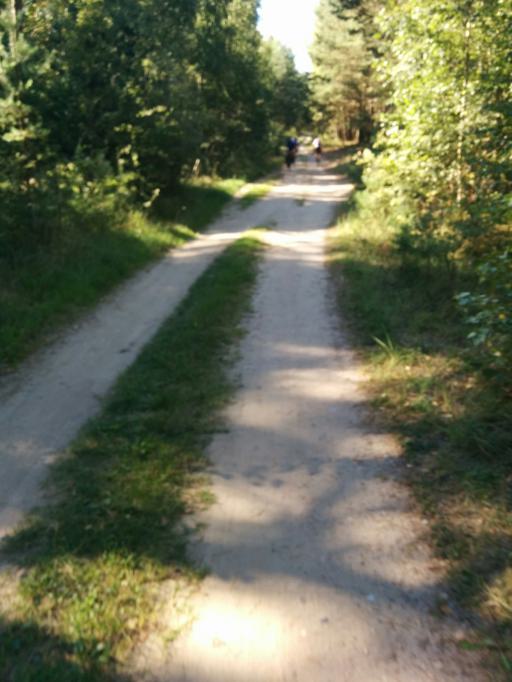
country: DE
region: Brandenburg
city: Templin
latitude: 53.0877
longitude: 13.4124
